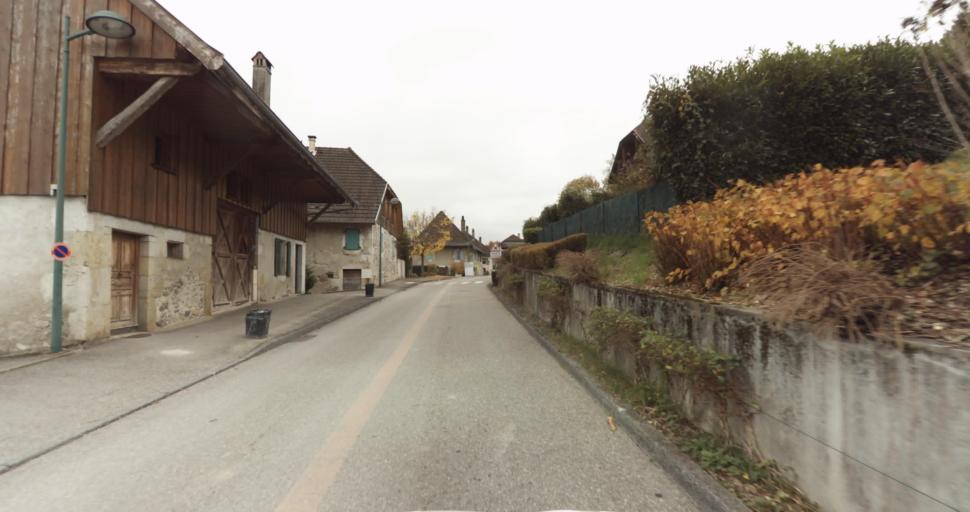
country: FR
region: Rhone-Alpes
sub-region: Departement de la Haute-Savoie
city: Saint-Jorioz
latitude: 45.8344
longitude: 6.1507
